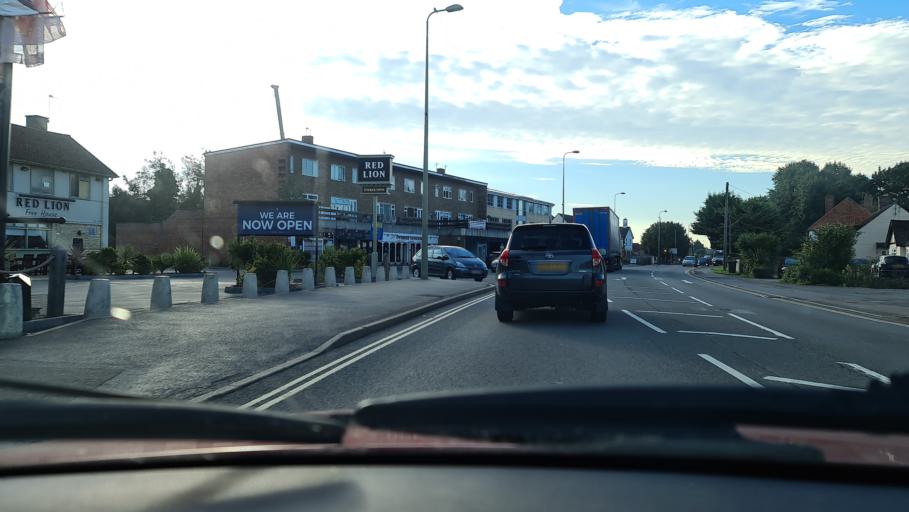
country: GB
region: England
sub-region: Oxfordshire
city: Kidlington
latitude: 51.8228
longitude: -1.2899
